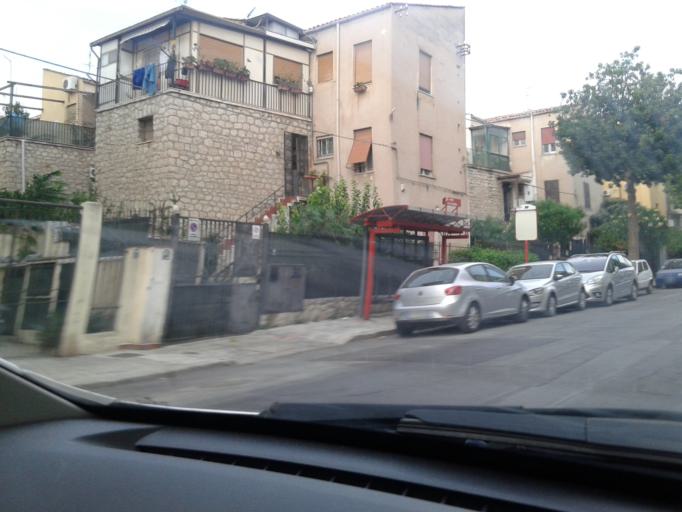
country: IT
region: Sicily
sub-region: Palermo
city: Palermo
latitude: 38.1105
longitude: 13.3344
